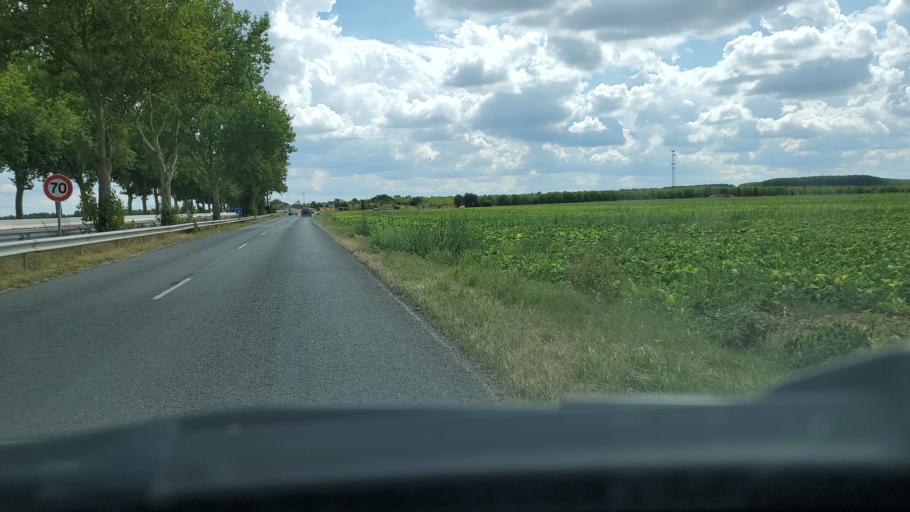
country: FR
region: Ile-de-France
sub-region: Departement de Seine-et-Marne
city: Nanteuil-les-Meaux
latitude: 48.9222
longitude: 2.8802
